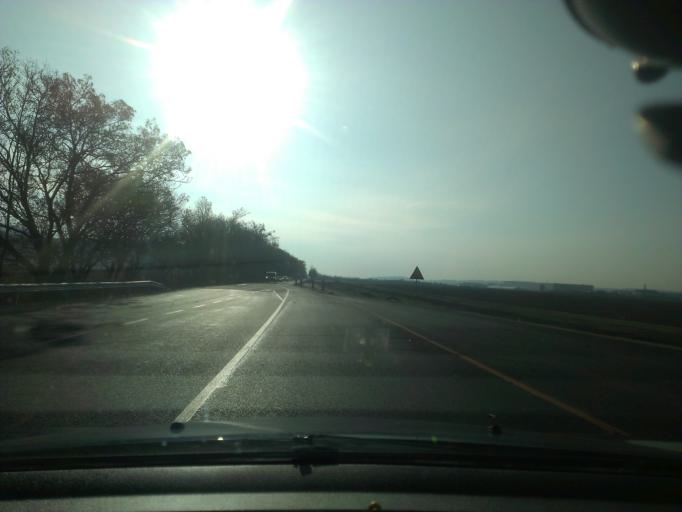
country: SK
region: Nitriansky
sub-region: Okres Nitra
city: Nitra
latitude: 48.3661
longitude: 18.0448
